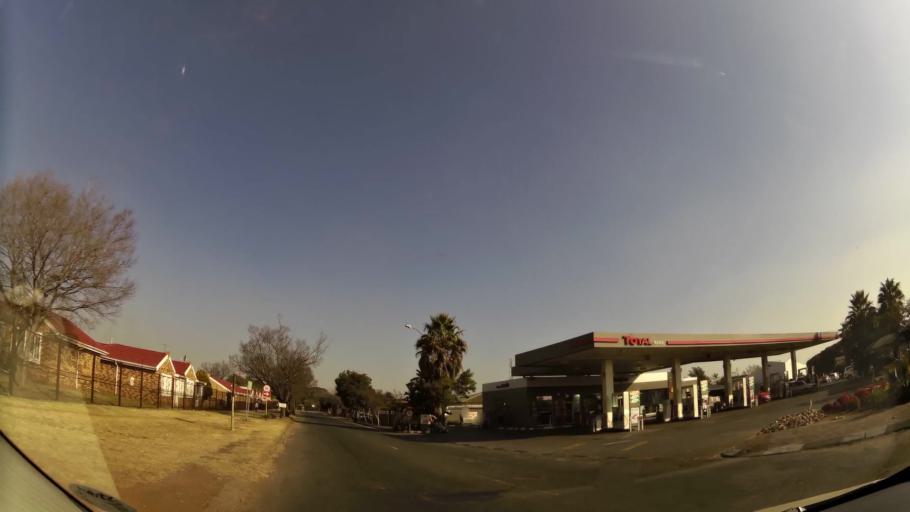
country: ZA
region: Gauteng
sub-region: West Rand District Municipality
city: Randfontein
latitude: -26.1757
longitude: 27.7076
